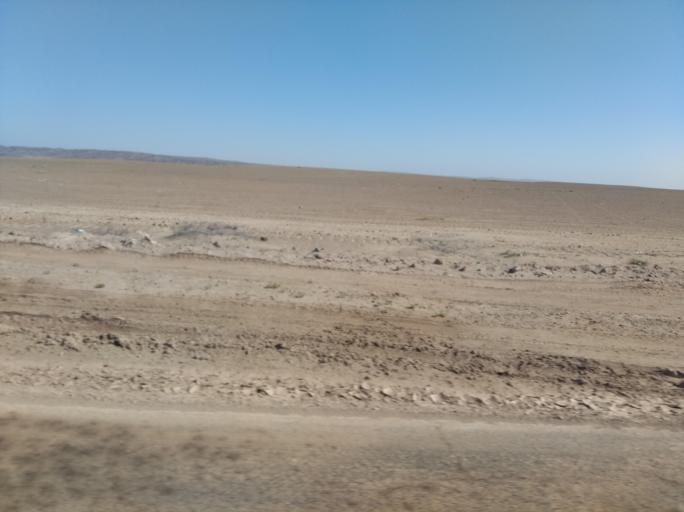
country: CL
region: Atacama
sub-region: Provincia de Copiapo
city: Copiapo
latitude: -27.3244
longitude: -70.8066
